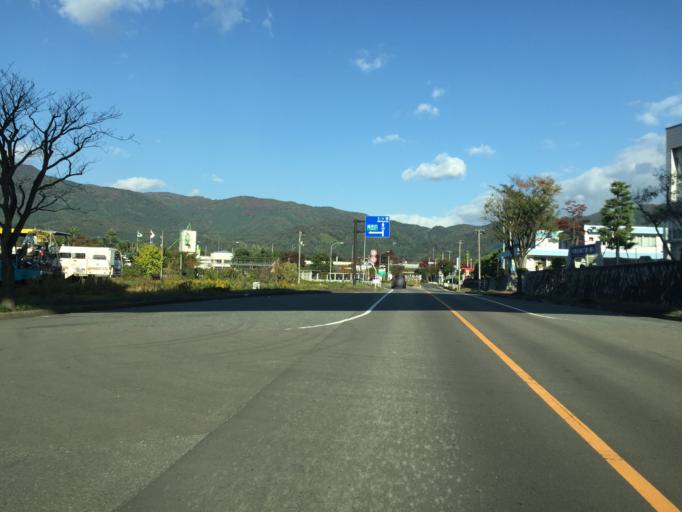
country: JP
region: Fukushima
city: Hobaramachi
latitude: 37.8787
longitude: 140.5354
